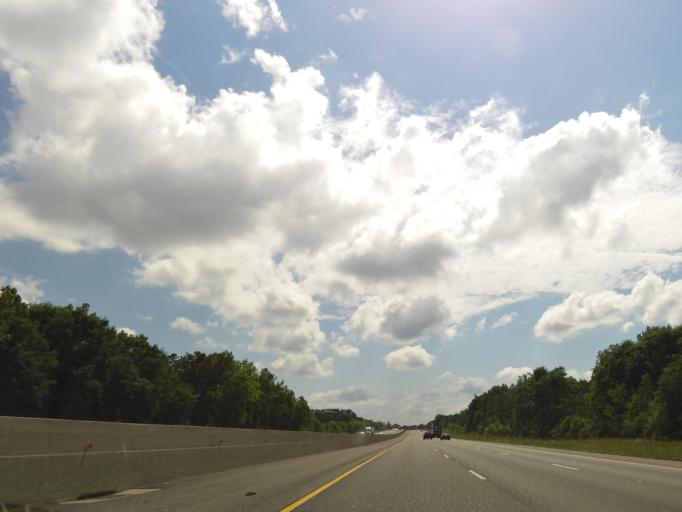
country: US
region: Alabama
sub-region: Calhoun County
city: Oxford
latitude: 33.5945
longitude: -85.8570
